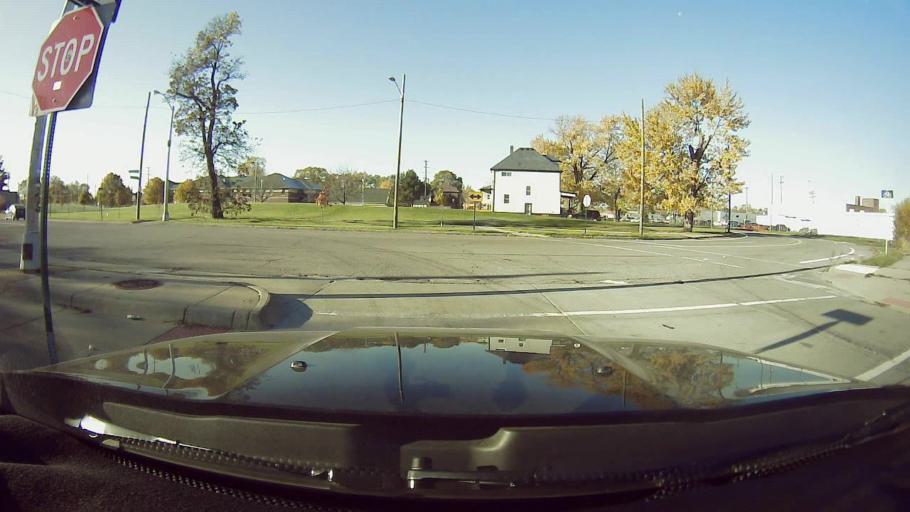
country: US
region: Michigan
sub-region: Wayne County
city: Detroit
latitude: 42.3336
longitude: -83.0966
